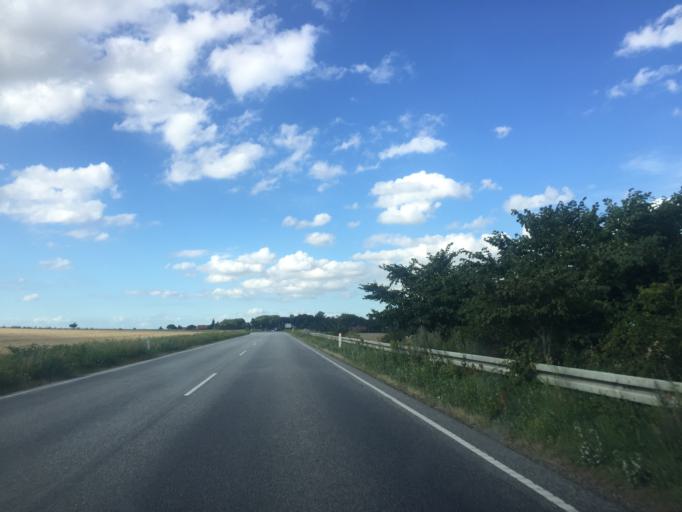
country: DK
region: Zealand
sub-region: Guldborgsund Kommune
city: Nykobing Falster
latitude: 54.7021
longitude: 11.9163
